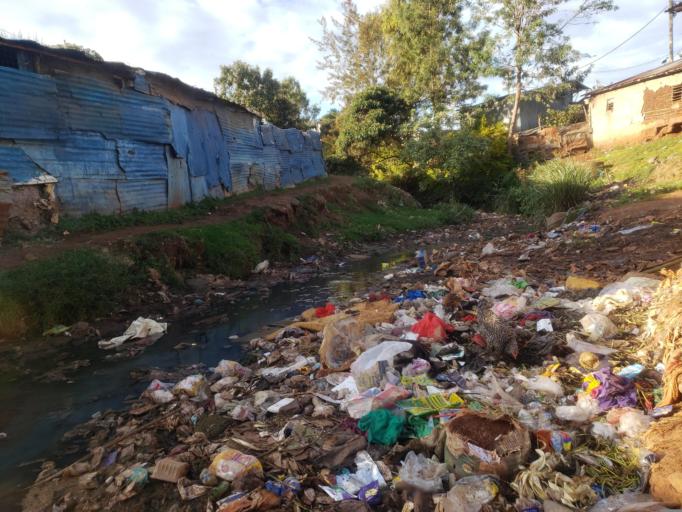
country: KE
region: Nairobi Area
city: Nairobi
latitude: -1.3101
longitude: 36.7719
